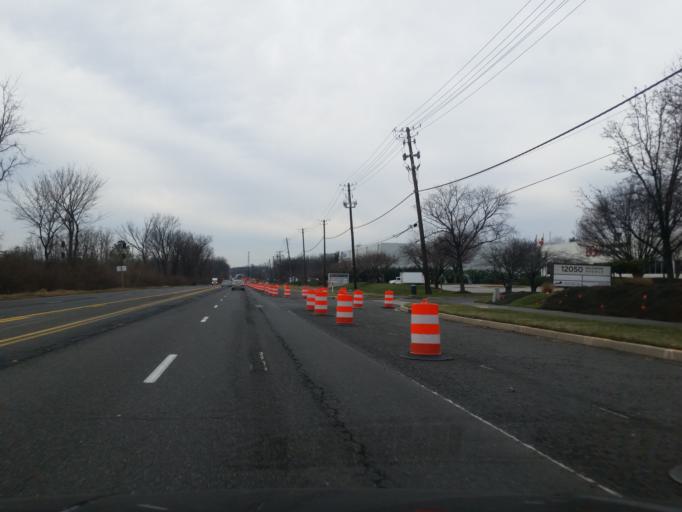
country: US
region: Maryland
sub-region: Prince George's County
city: Beltsville
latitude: 39.0558
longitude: -76.8921
